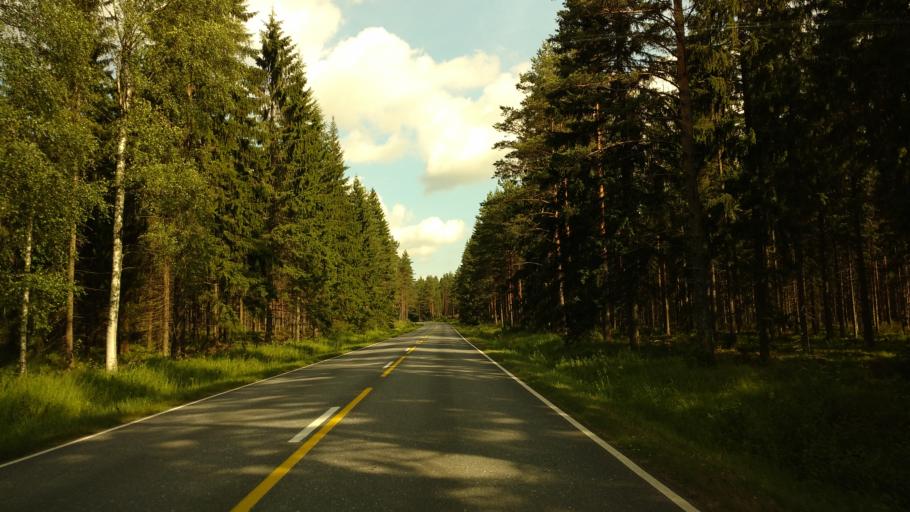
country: FI
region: Varsinais-Suomi
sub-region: Loimaa
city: Koski Tl
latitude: 60.6104
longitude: 23.1204
